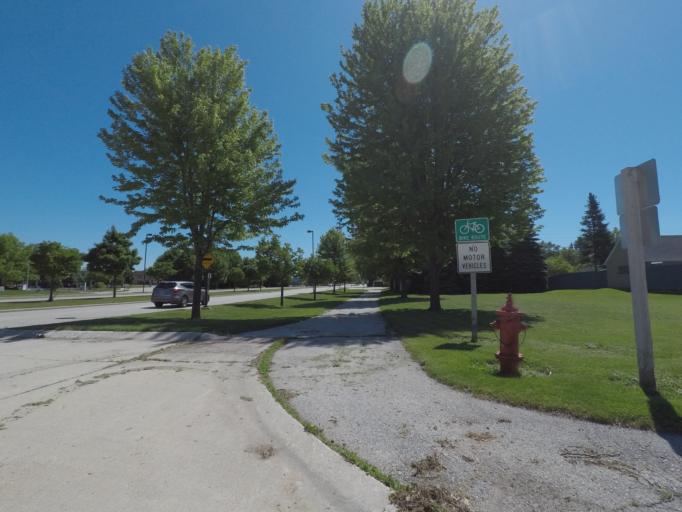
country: US
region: Wisconsin
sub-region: Sheboygan County
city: Sheboygan
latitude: 43.7562
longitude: -87.7421
